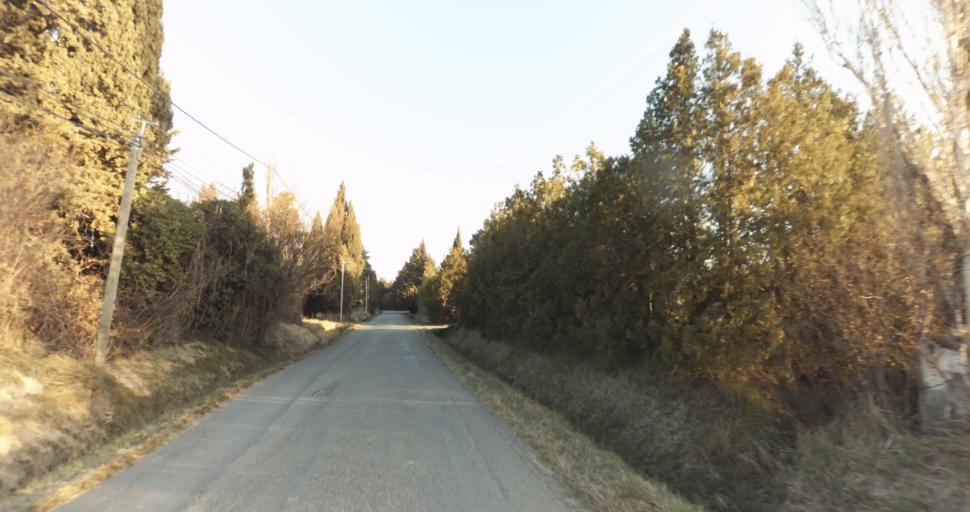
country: FR
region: Provence-Alpes-Cote d'Azur
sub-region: Departement des Bouches-du-Rhone
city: Barbentane
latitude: 43.8870
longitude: 4.7726
